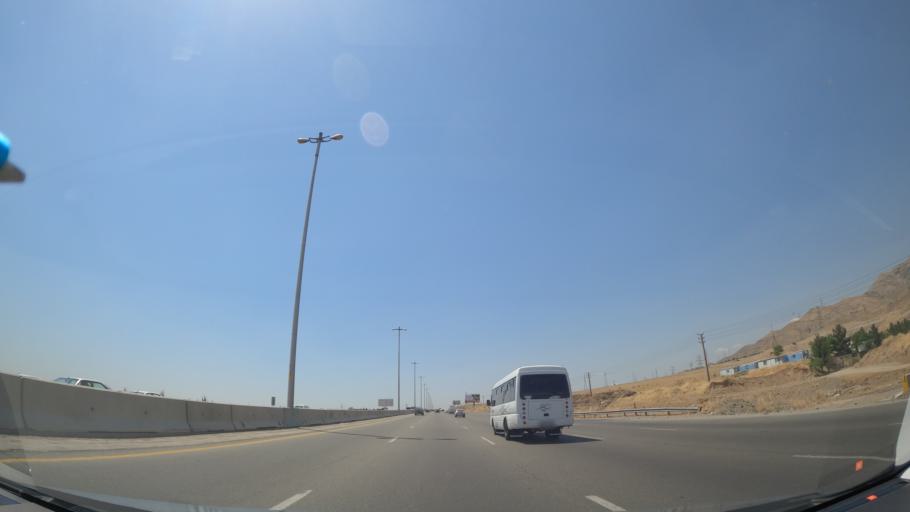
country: IR
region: Tehran
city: Shahr-e Qods
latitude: 35.7656
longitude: 51.0555
